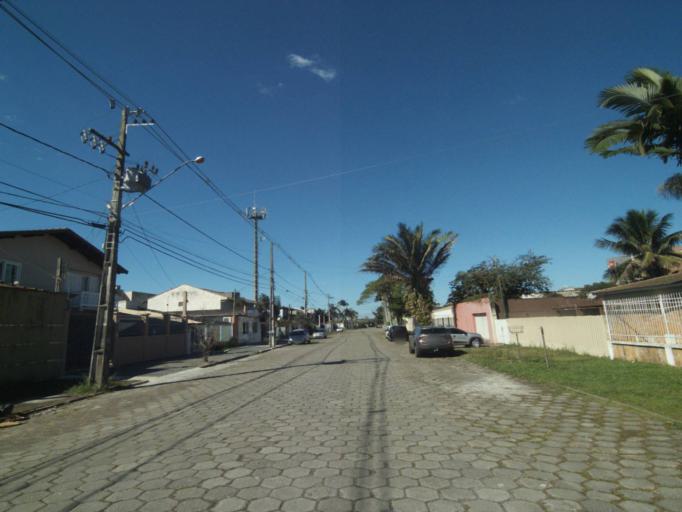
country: BR
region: Parana
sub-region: Paranagua
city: Paranagua
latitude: -25.5138
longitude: -48.5024
